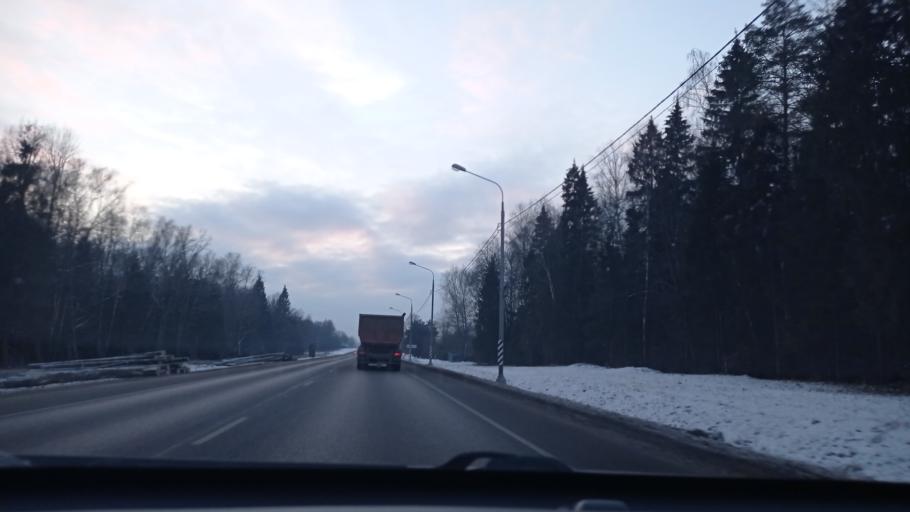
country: RU
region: Kaluga
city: Zhukovo
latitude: 55.1535
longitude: 36.8219
